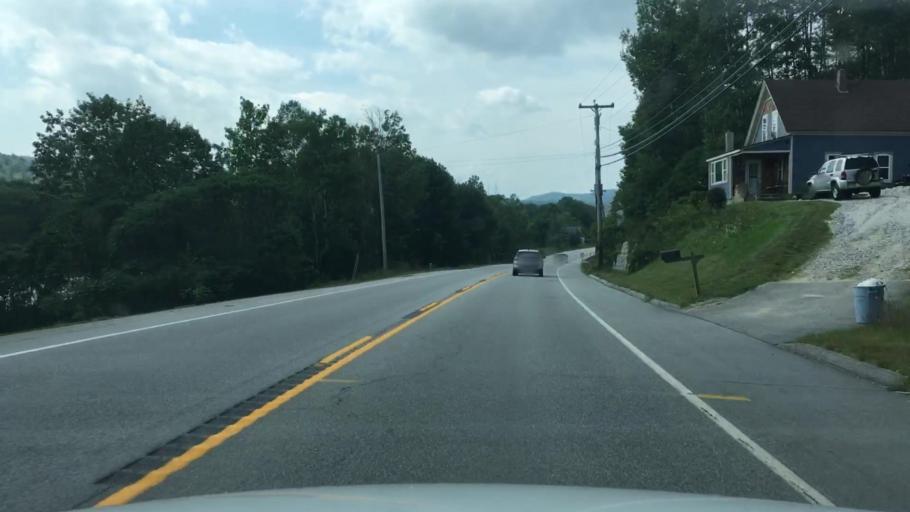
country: US
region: Maine
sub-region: Oxford County
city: Rumford
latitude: 44.5095
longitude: -70.5765
